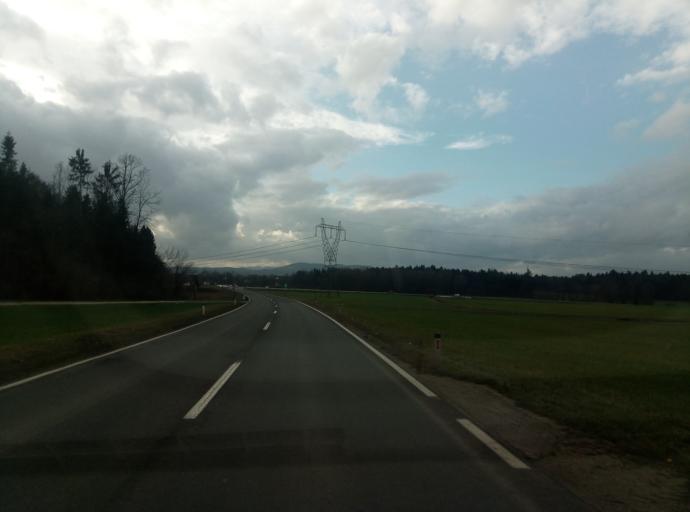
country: SI
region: Domzale
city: Dob
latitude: 46.1613
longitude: 14.6518
